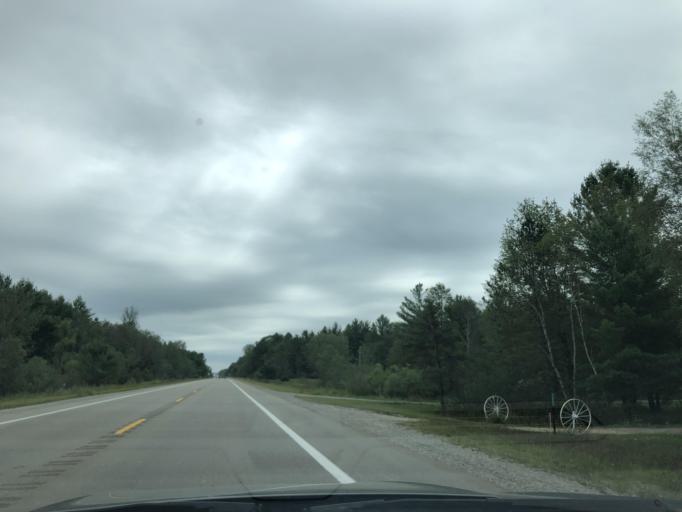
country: US
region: Michigan
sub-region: Clare County
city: Harrison
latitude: 44.0311
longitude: -84.9953
